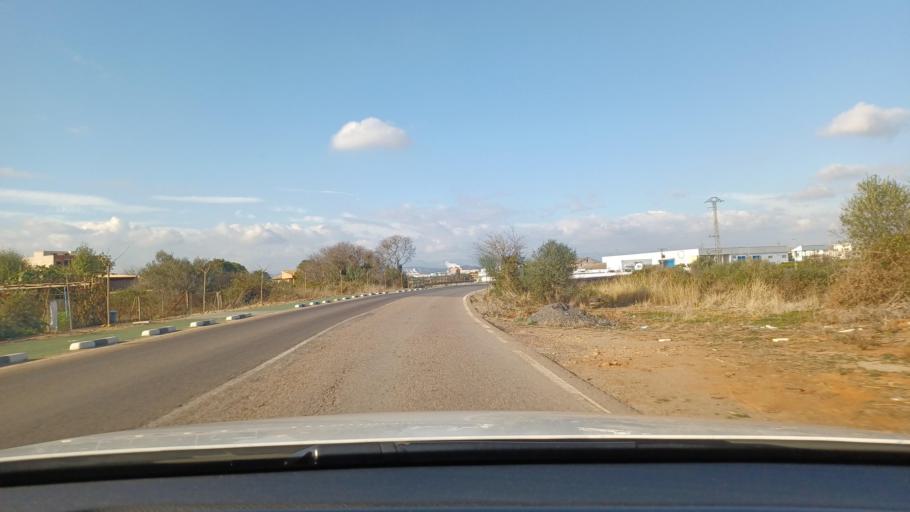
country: ES
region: Valencia
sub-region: Provincia de Castello
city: Betxi
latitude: 39.9296
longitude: -0.1943
